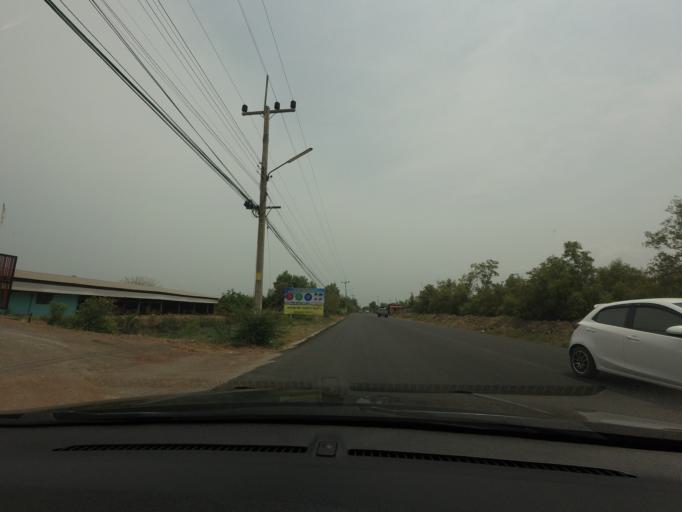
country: TH
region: Samut Songkhram
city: Amphawa
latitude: 13.3487
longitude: 99.9322
